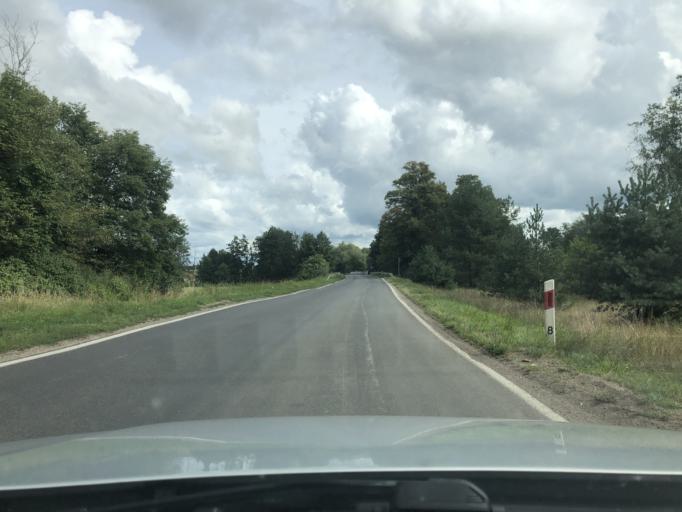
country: PL
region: Greater Poland Voivodeship
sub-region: Powiat czarnkowsko-trzcianecki
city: Krzyz Wielkopolski
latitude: 52.8713
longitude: 15.9796
